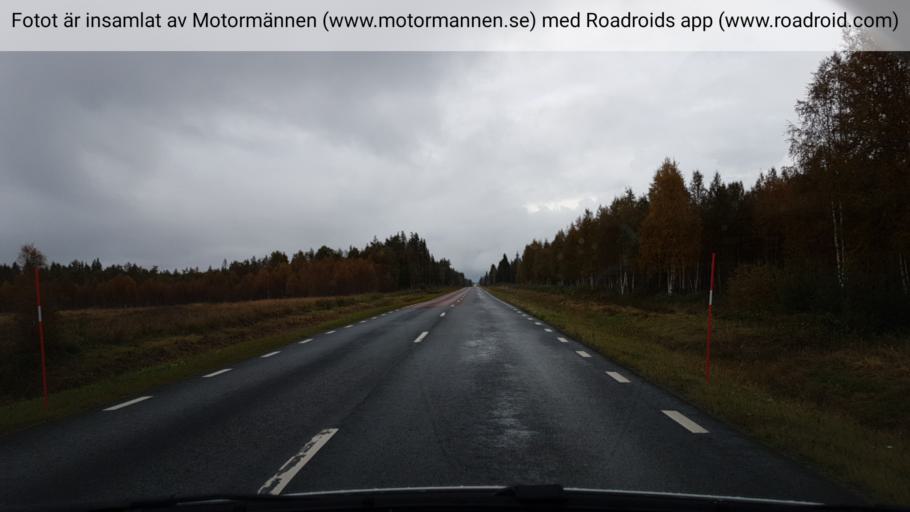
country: SE
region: Jaemtland
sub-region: Stroemsunds Kommun
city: Stroemsund
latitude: 63.7969
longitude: 15.5155
